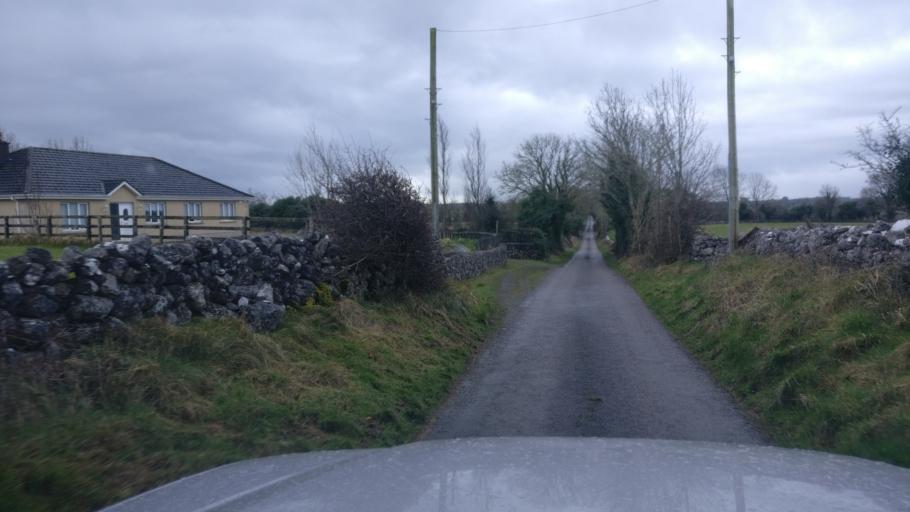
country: IE
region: Connaught
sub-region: County Galway
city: Athenry
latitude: 53.1933
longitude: -8.6871
